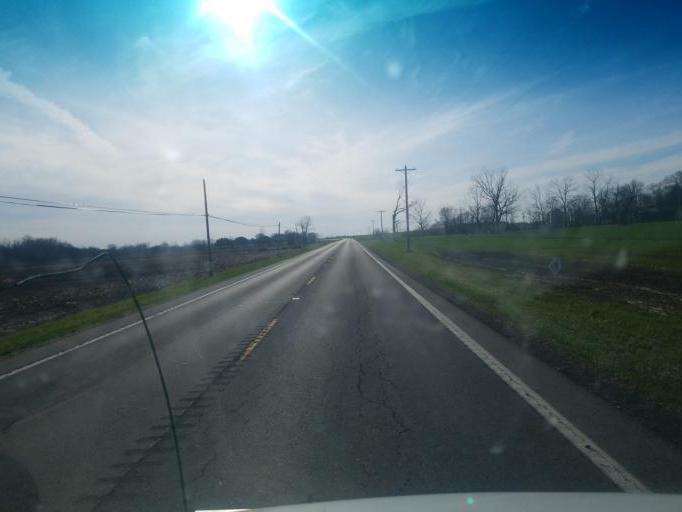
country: US
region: Ohio
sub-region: Logan County
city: De Graff
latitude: 40.3668
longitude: -83.8526
